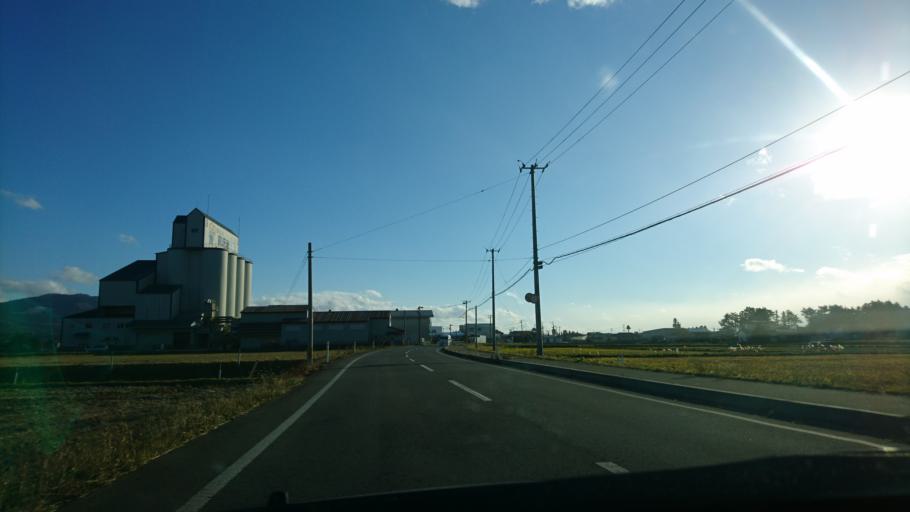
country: JP
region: Iwate
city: Mizusawa
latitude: 39.0697
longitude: 141.1469
